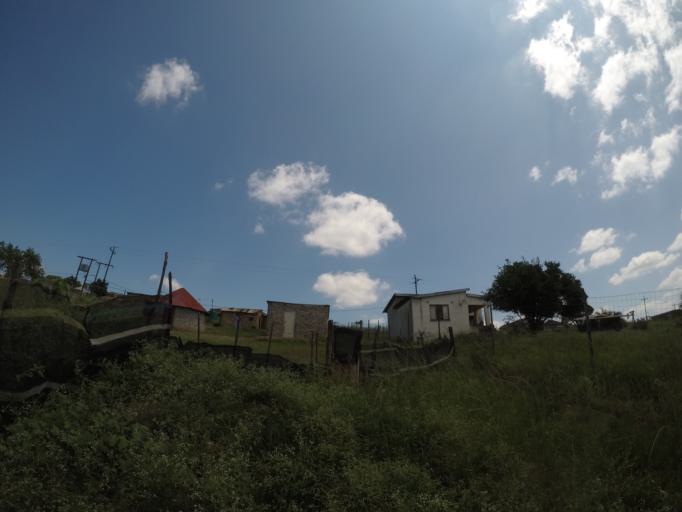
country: ZA
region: KwaZulu-Natal
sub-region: uThungulu District Municipality
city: Empangeni
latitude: -28.6055
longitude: 31.7358
